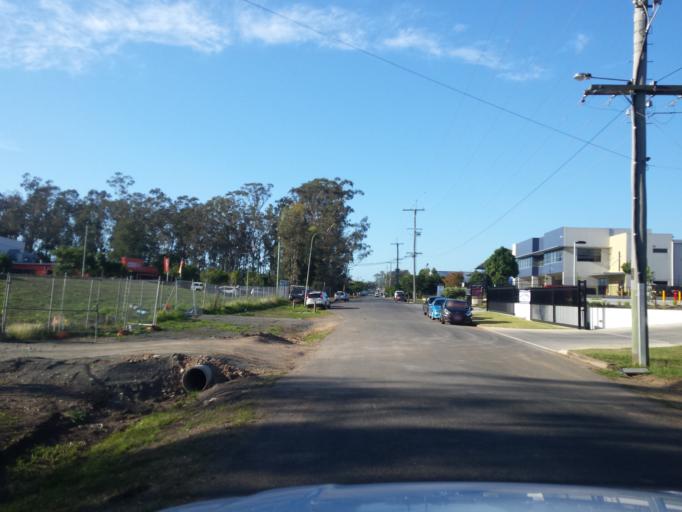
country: AU
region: Queensland
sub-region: Logan
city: Slacks Creek
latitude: -27.6587
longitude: 153.1340
